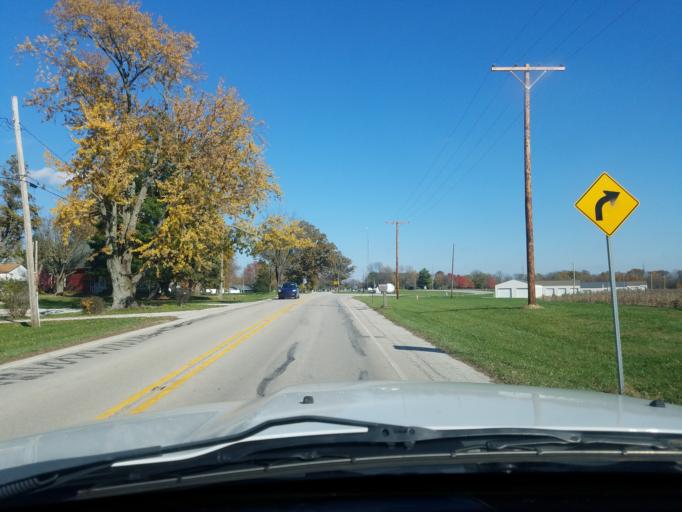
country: US
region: Indiana
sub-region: Hendricks County
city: Pittsboro
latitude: 39.9283
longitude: -86.6239
